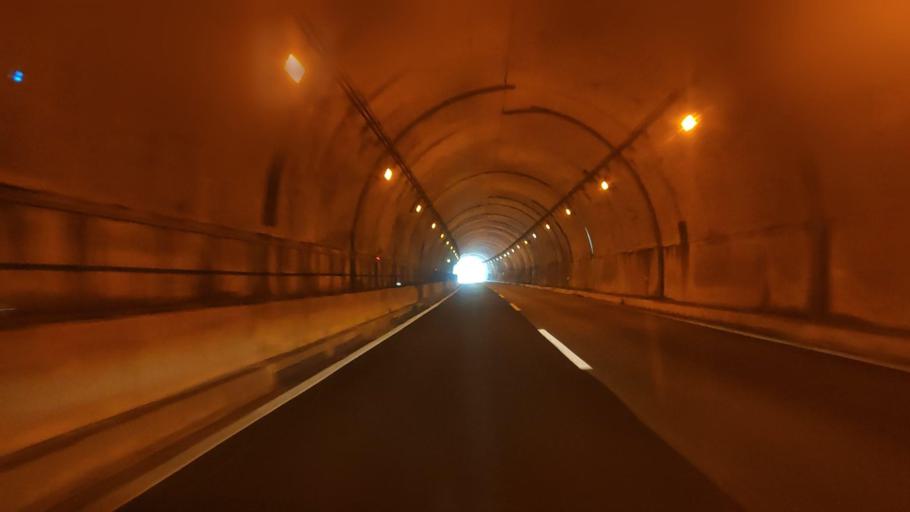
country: JP
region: Miyazaki
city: Miyazaki-shi
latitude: 31.8197
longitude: 131.2607
